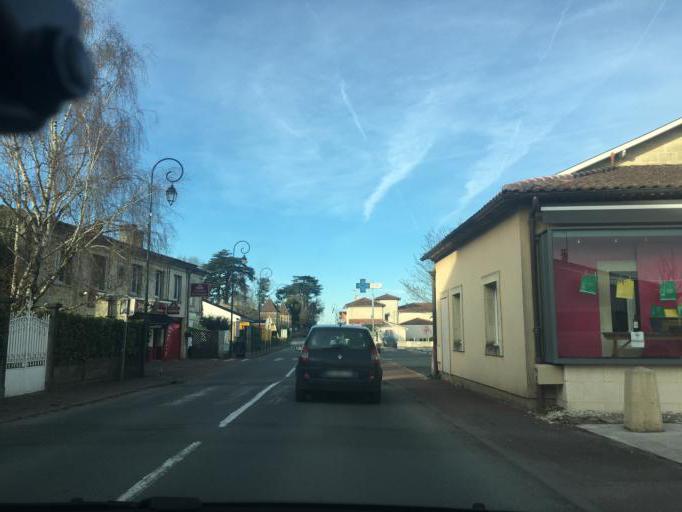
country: FR
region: Aquitaine
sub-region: Departement de la Gironde
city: Saint-Germain-du-Puch
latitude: 44.8549
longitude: -0.3239
